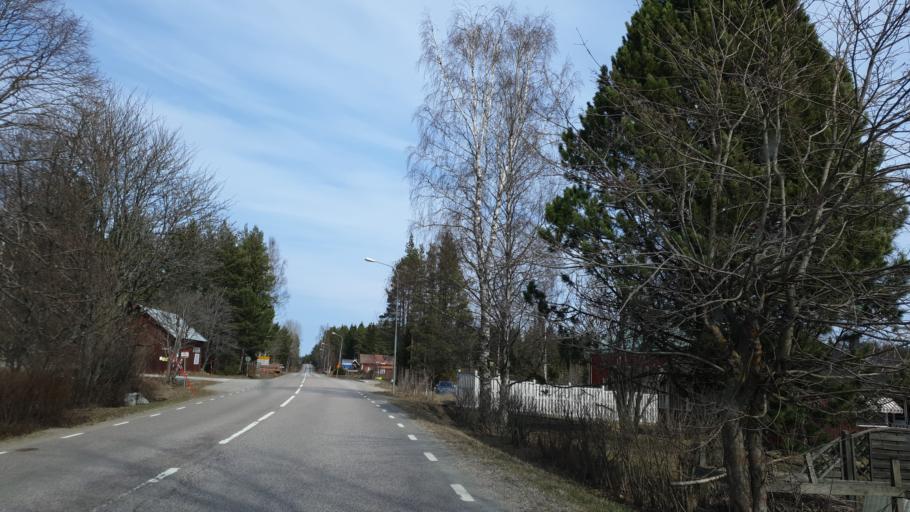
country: SE
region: Gaevleborg
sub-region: Gavle Kommun
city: Norrsundet
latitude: 61.0033
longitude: 17.1252
